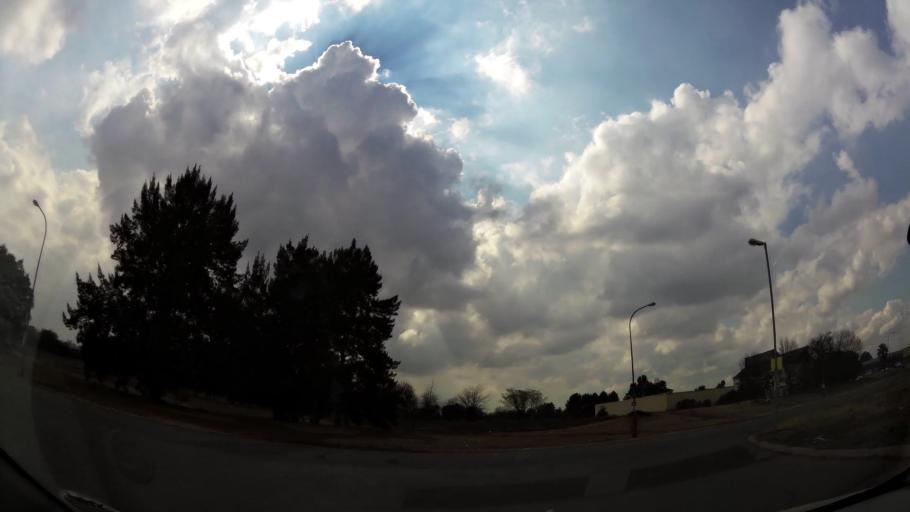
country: ZA
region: Gauteng
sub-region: Sedibeng District Municipality
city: Vereeniging
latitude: -26.6560
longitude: 27.9347
